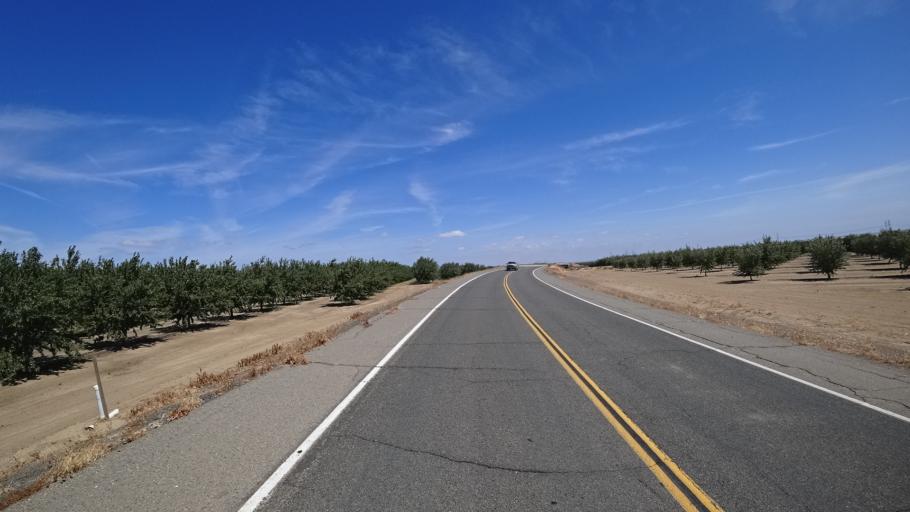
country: US
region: California
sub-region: Kings County
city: Kettleman City
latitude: 35.9575
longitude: -119.9374
